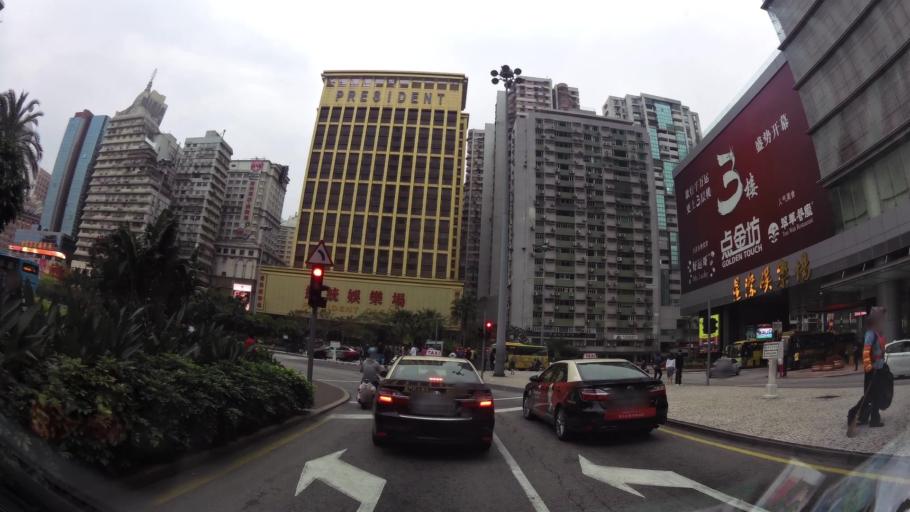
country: MO
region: Macau
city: Macau
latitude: 22.1894
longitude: 113.5475
